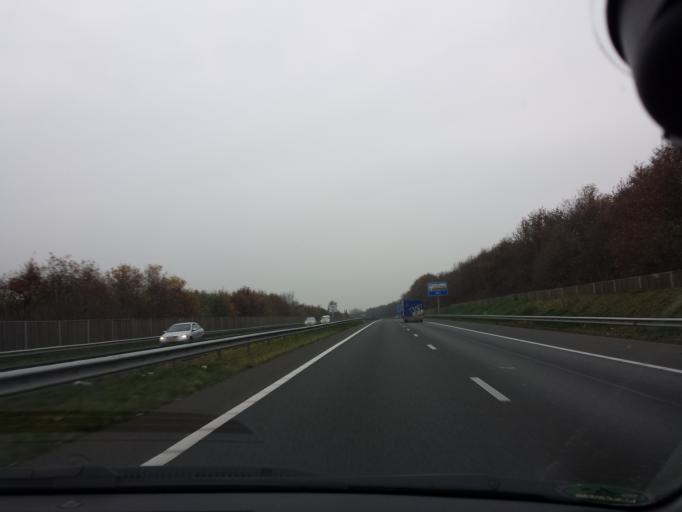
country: NL
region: Limburg
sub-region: Gemeente Venray
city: Venray
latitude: 51.5316
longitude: 5.9997
